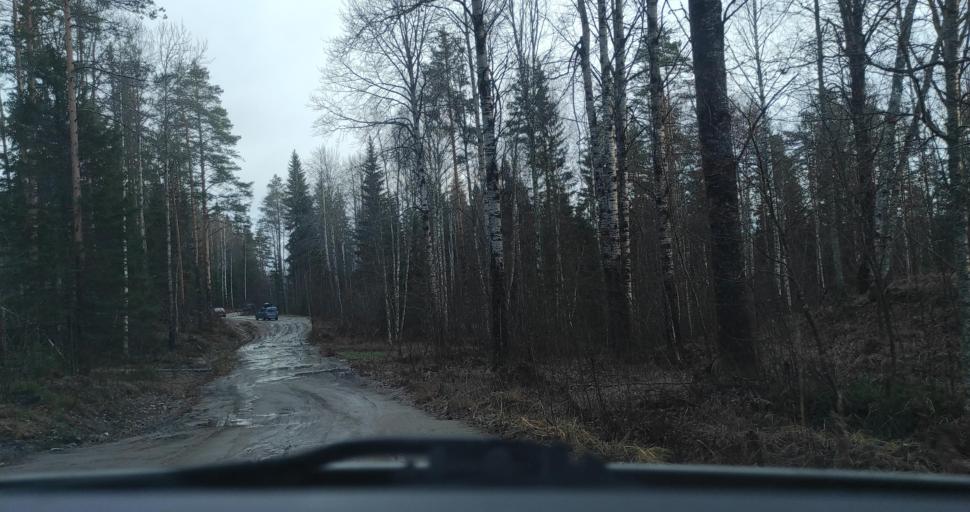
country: RU
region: Republic of Karelia
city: Pitkyaranta
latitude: 61.7441
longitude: 31.3942
